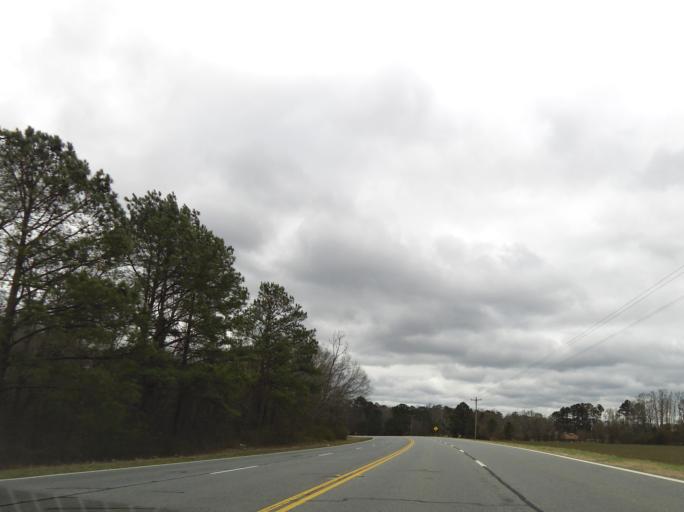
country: US
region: Georgia
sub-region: Bleckley County
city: Cochran
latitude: 32.4388
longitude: -83.3770
